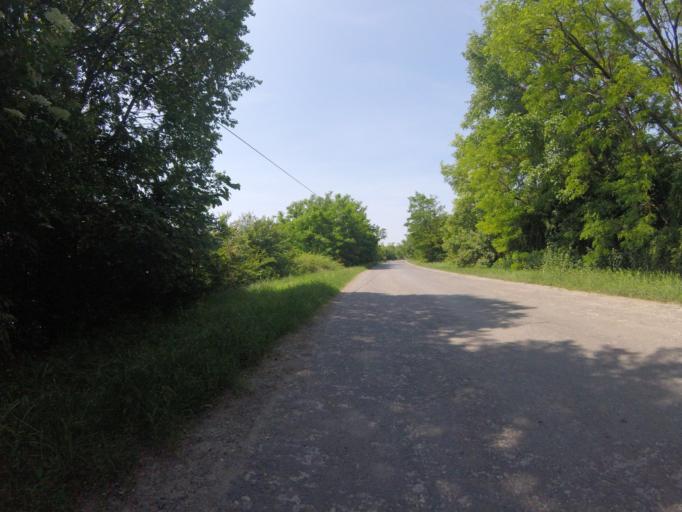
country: HU
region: Tolna
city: Bolcske
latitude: 46.7296
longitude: 18.9354
